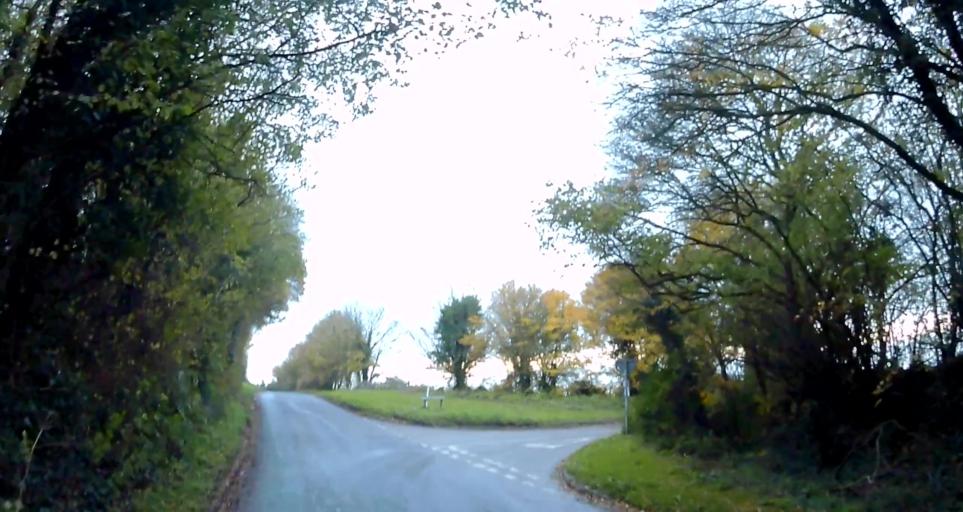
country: GB
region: England
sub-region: Hampshire
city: Odiham
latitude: 51.2540
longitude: -0.9590
